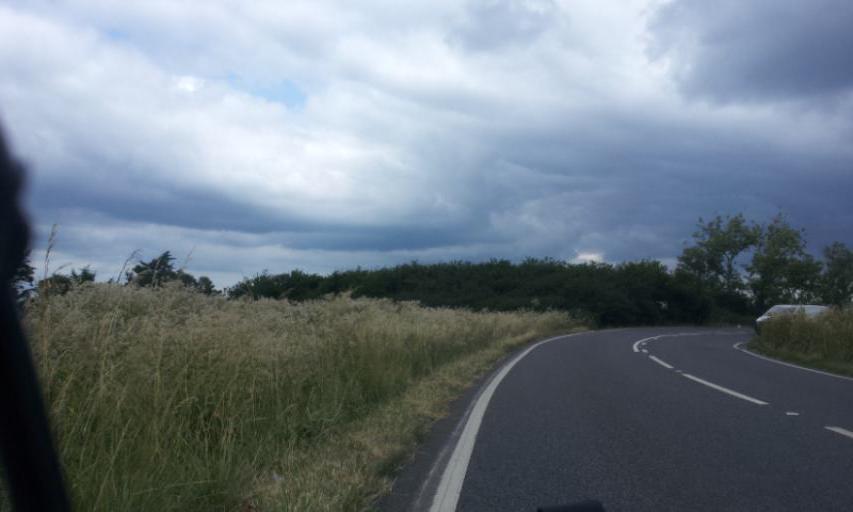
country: GB
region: England
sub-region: Kent
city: Tankerton
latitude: 51.3635
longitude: 1.0805
